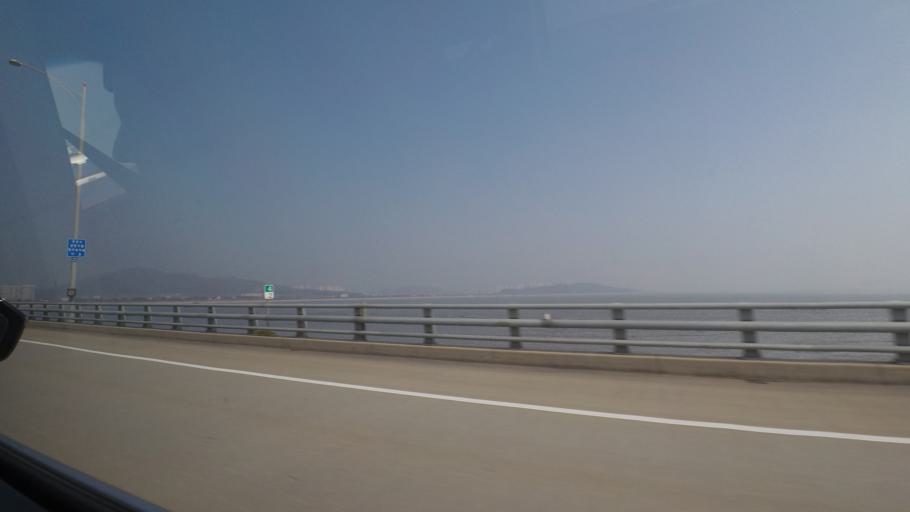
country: KR
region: Incheon
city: Incheon
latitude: 37.4574
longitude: 126.5230
